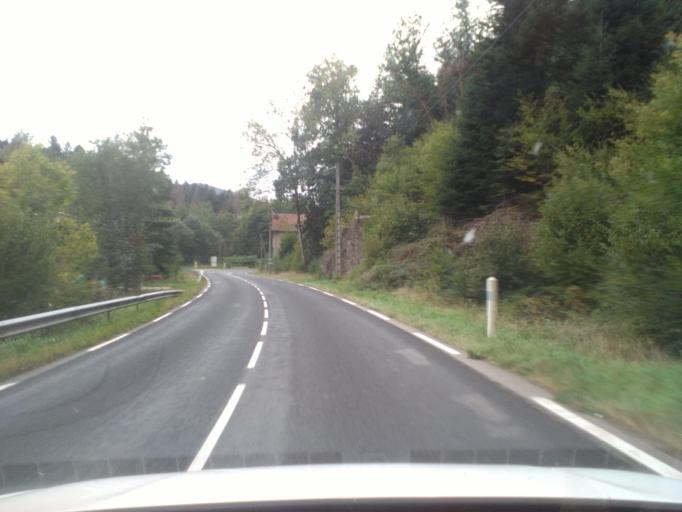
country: FR
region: Lorraine
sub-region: Departement des Vosges
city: Senones
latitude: 48.4039
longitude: 7.0197
